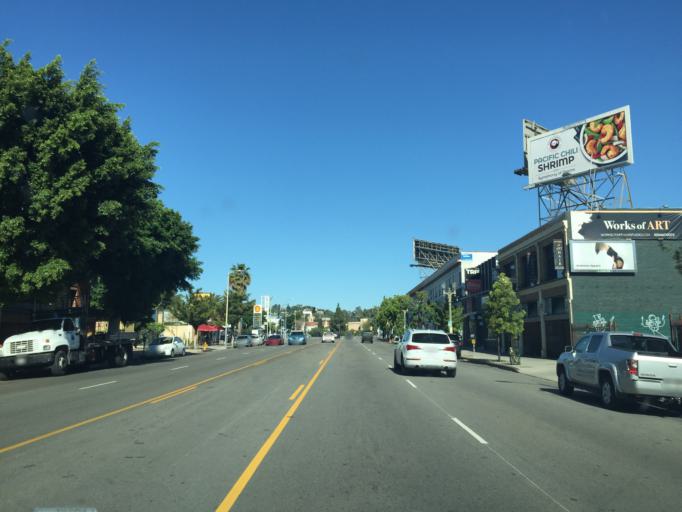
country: US
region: California
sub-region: Los Angeles County
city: Silver Lake
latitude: 34.1003
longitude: -118.2903
